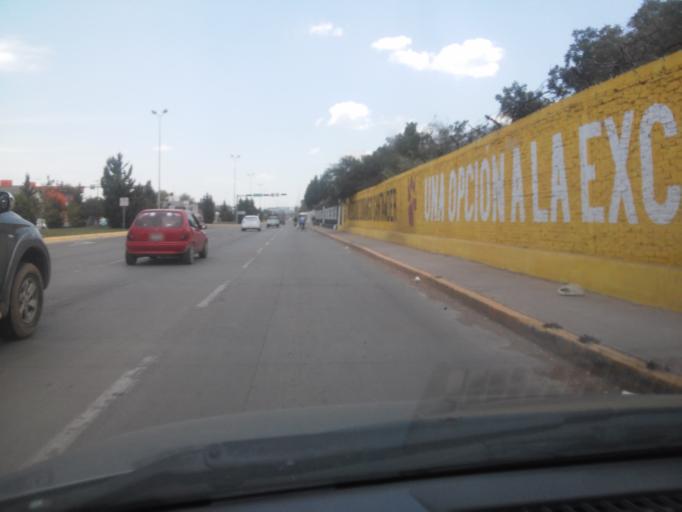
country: MX
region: Durango
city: Victoria de Durango
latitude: 24.0579
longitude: -104.6379
